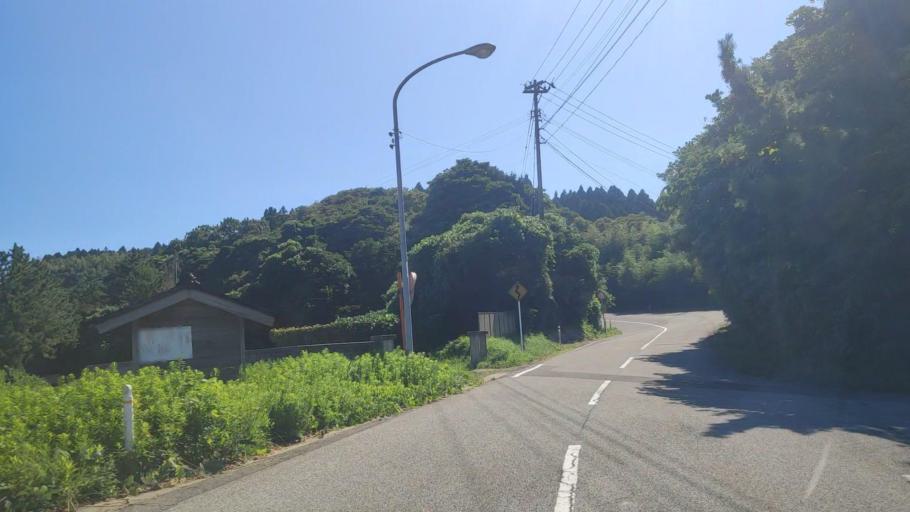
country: JP
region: Ishikawa
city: Nanao
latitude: 37.5220
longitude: 137.3266
